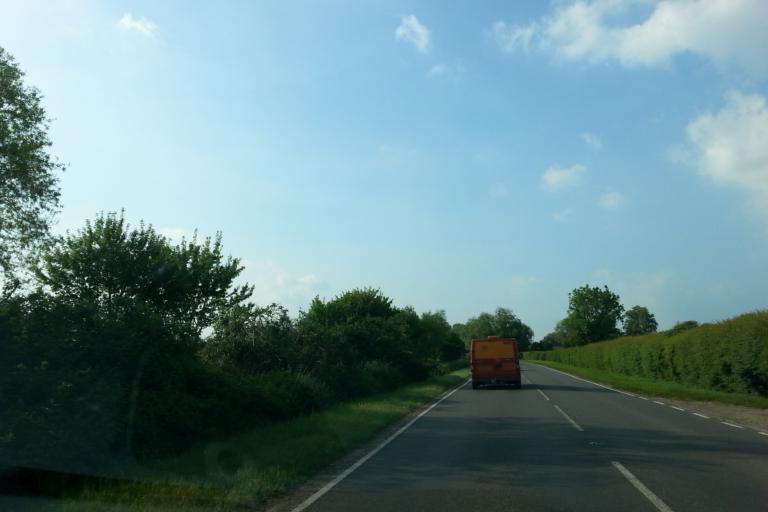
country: GB
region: England
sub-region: Cambridgeshire
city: Earith
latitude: 52.3437
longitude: 0.0601
